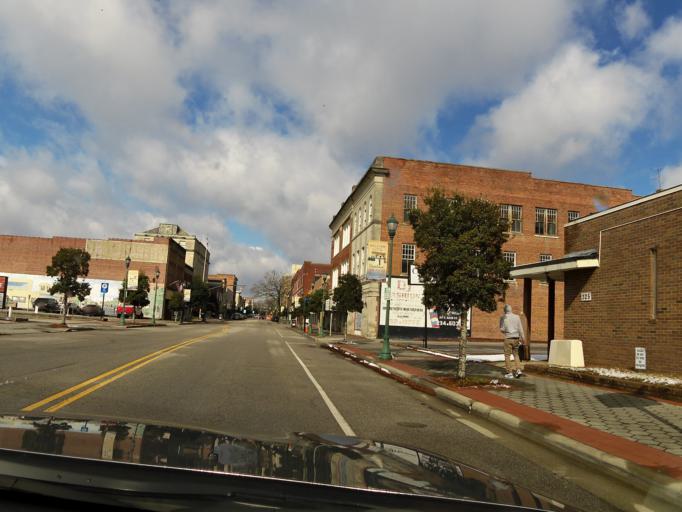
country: US
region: North Carolina
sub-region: Wilson County
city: Wilson
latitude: 35.7235
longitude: -77.9087
